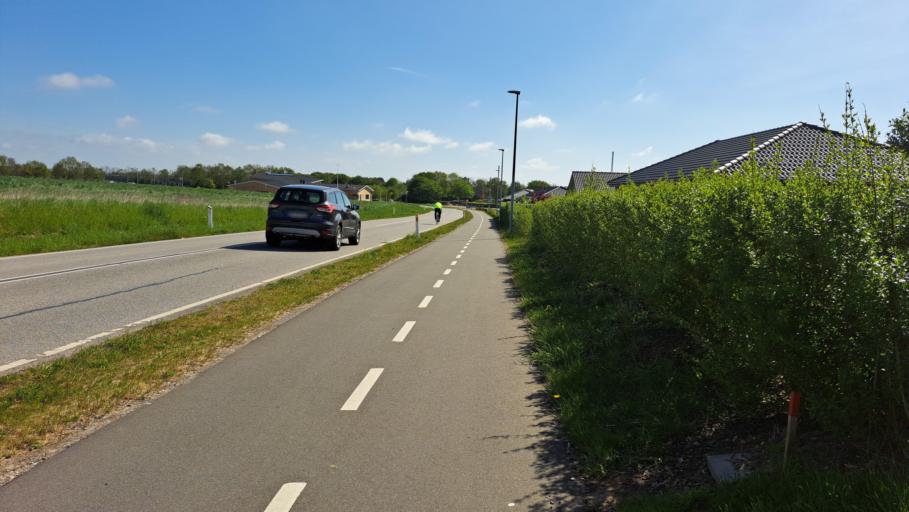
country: DK
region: Central Jutland
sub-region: Hedensted Kommune
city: Hedensted
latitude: 55.7982
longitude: 9.6490
